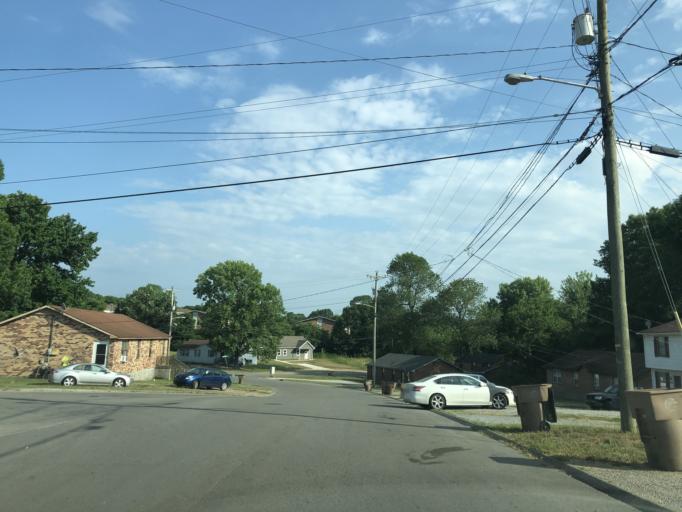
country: US
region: Tennessee
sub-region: Davidson County
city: Nashville
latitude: 36.2215
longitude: -86.8027
